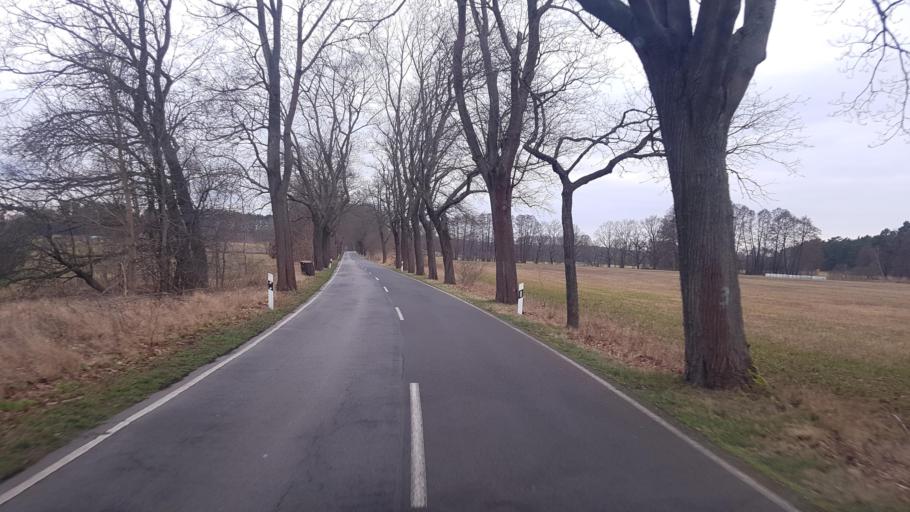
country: DE
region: Brandenburg
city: Halbe
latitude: 52.0838
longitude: 13.7066
